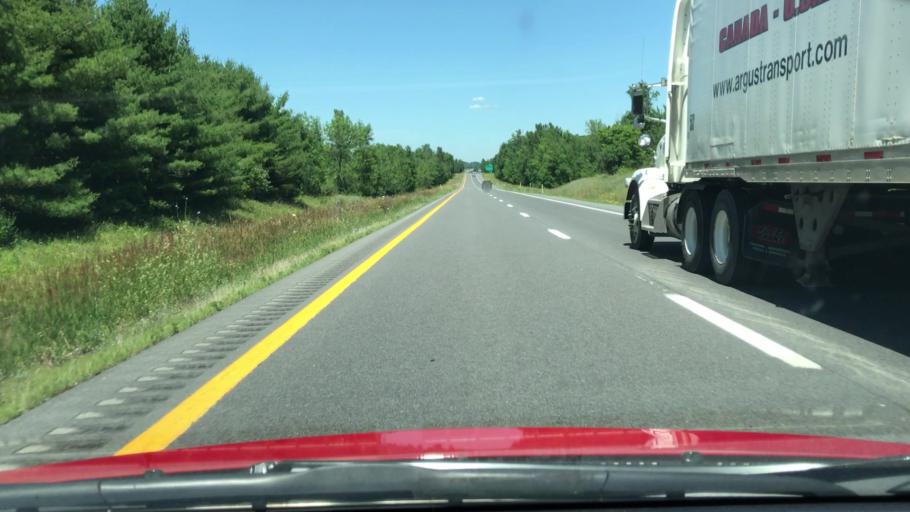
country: US
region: New York
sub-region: Clinton County
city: Cumberland Head
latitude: 44.7568
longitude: -73.4290
